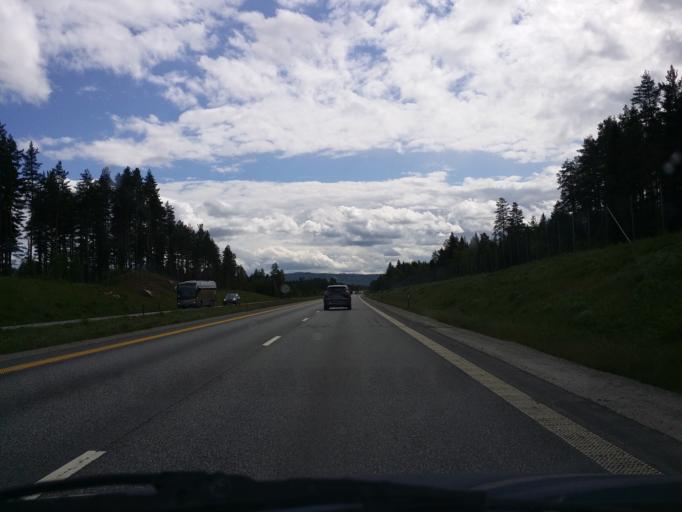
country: NO
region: Hedmark
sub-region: Stange
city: Stange
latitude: 60.6729
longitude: 11.2873
